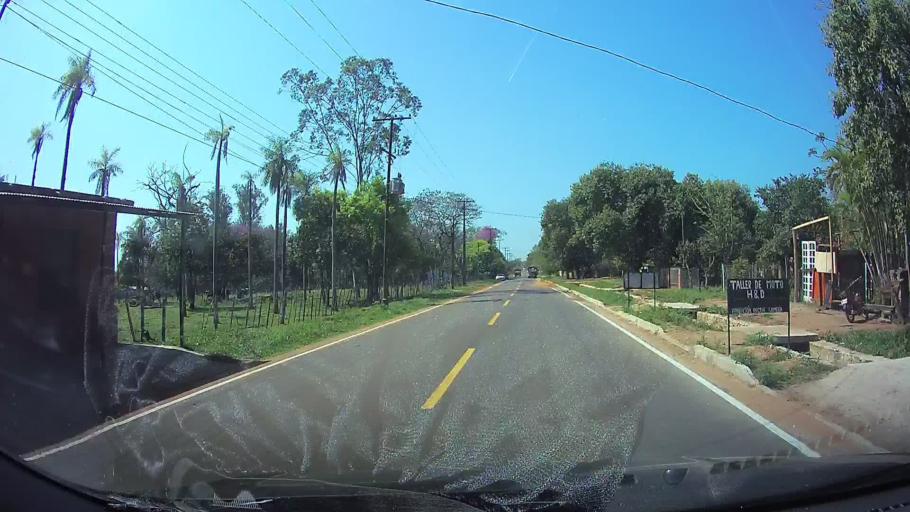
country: PY
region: Central
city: Limpio
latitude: -25.2258
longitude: -57.4884
